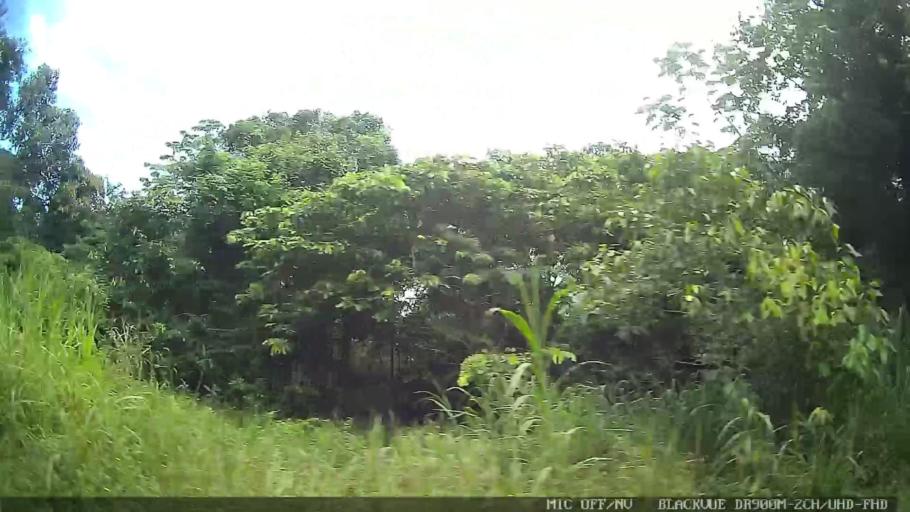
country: BR
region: Sao Paulo
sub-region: Iguape
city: Iguape
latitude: -24.6863
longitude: -47.4833
